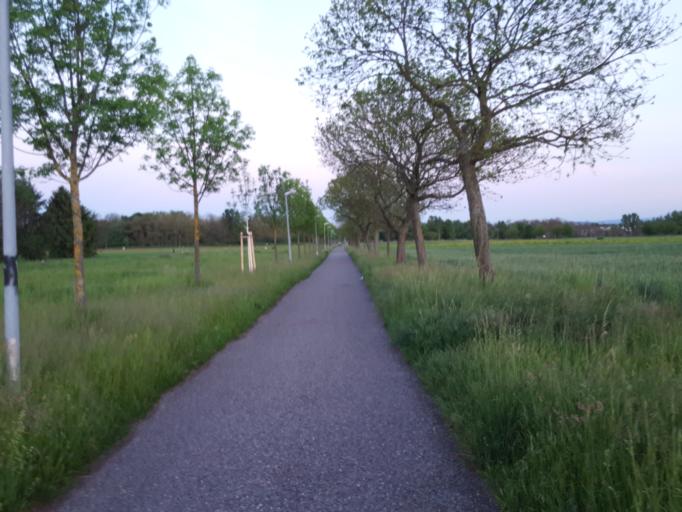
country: DE
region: Baden-Wuerttemberg
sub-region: Karlsruhe Region
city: Karlsruhe
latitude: 49.0427
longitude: 8.3841
